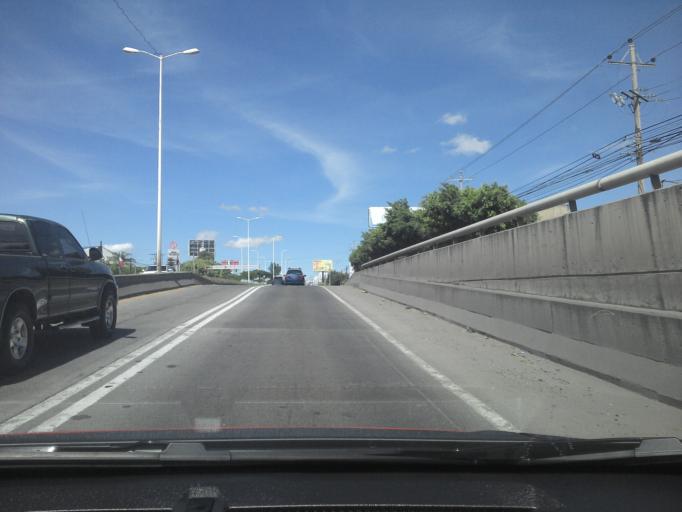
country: MX
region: Jalisco
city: Nuevo Mexico
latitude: 20.7107
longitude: -103.4679
